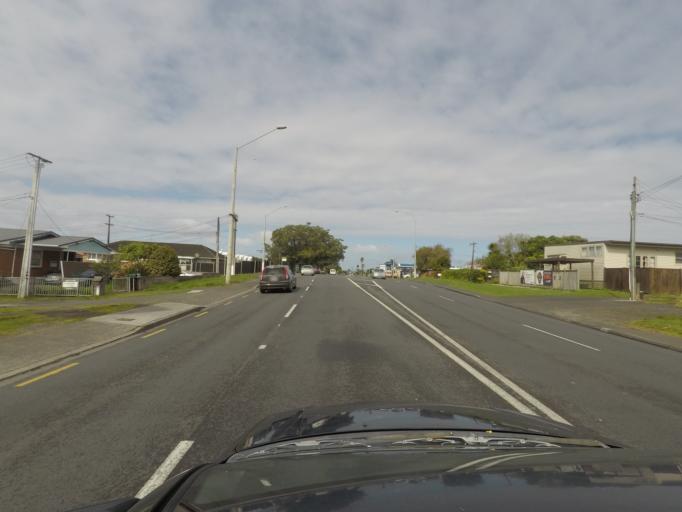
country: NZ
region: Auckland
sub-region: Auckland
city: Tamaki
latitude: -36.9071
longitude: 174.8397
